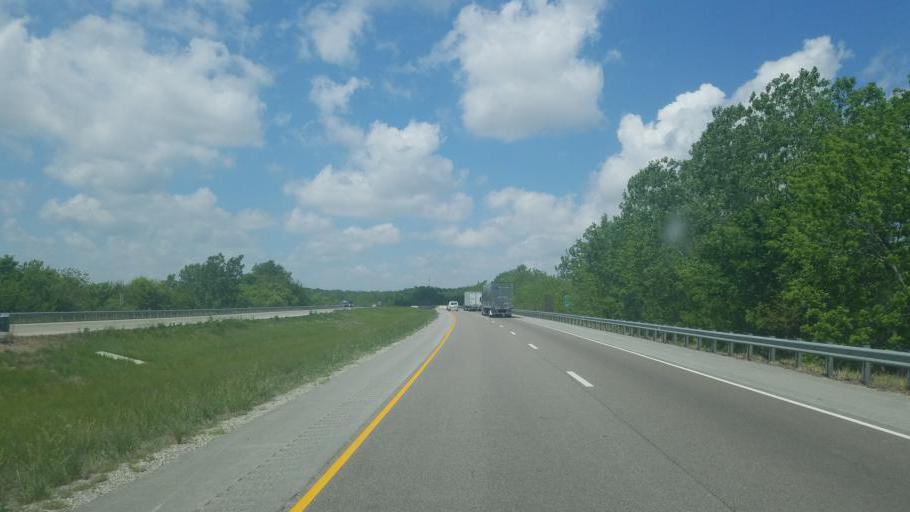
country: US
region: Illinois
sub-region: Cumberland County
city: Greenup
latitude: 39.2536
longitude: -88.1721
